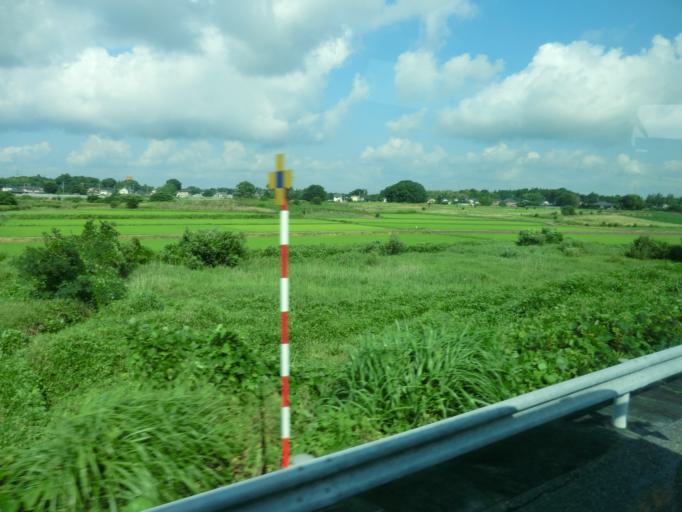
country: JP
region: Ibaraki
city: Ushiku
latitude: 36.0095
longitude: 140.1434
